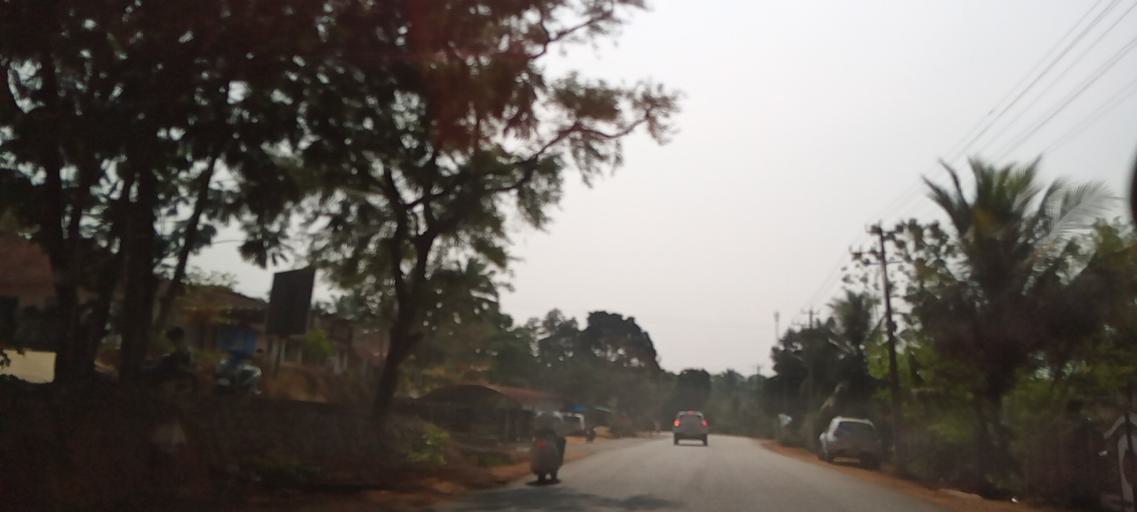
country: IN
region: Karnataka
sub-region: Udupi
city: Someshwar
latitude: 13.5281
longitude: 74.9225
